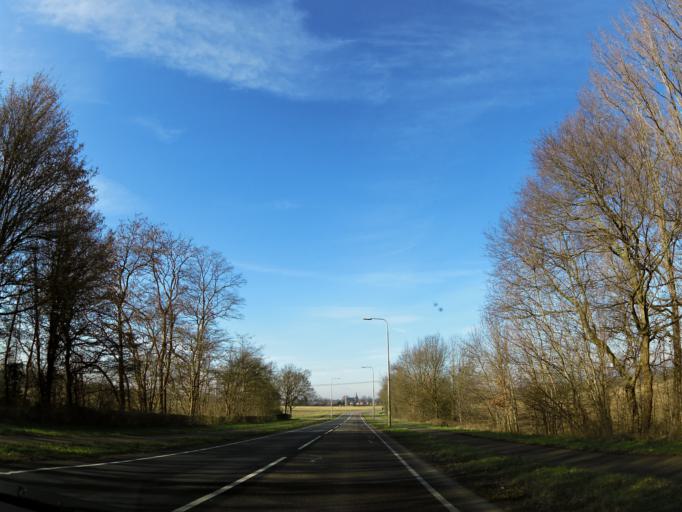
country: NL
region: Limburg
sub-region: Gemeente Sittard-Geleen
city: Born
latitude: 51.0372
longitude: 5.7949
